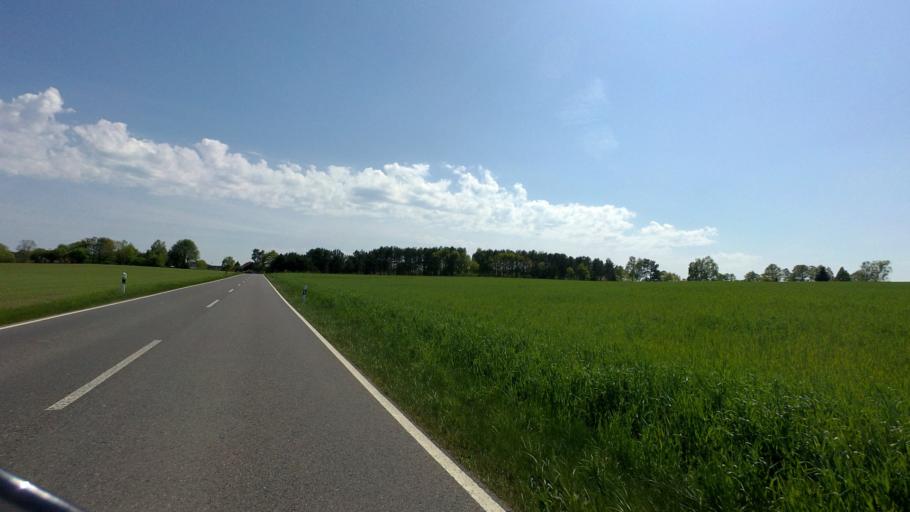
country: DE
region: Brandenburg
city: Lieberose
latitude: 51.9858
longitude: 14.2139
